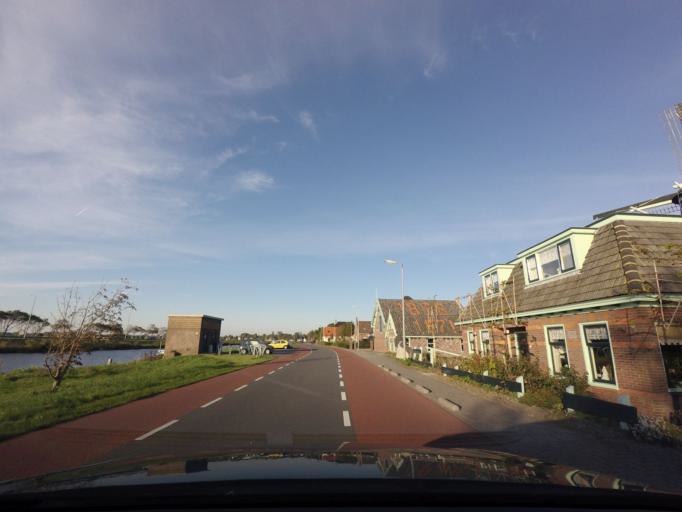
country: NL
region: North Holland
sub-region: Gemeente Alkmaar
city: Alkmaar
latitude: 52.6669
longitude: 4.7503
